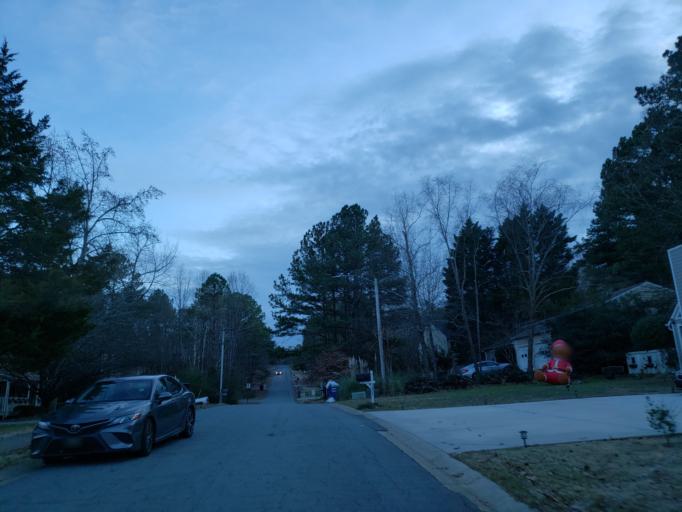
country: US
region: Georgia
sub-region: Cobb County
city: Kennesaw
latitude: 34.0469
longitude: -84.6451
